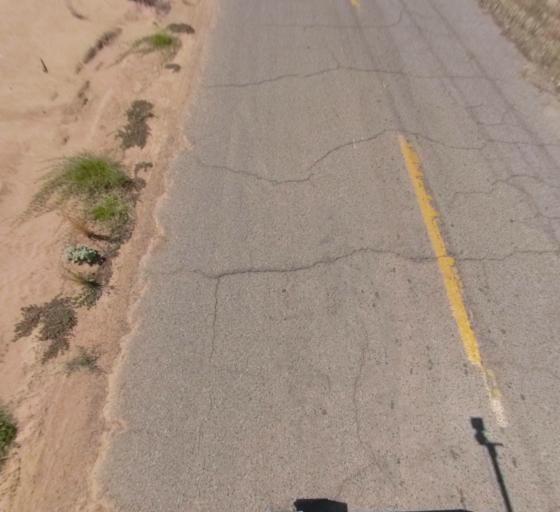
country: US
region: California
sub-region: Madera County
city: Parksdale
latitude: 36.9191
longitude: -119.9395
